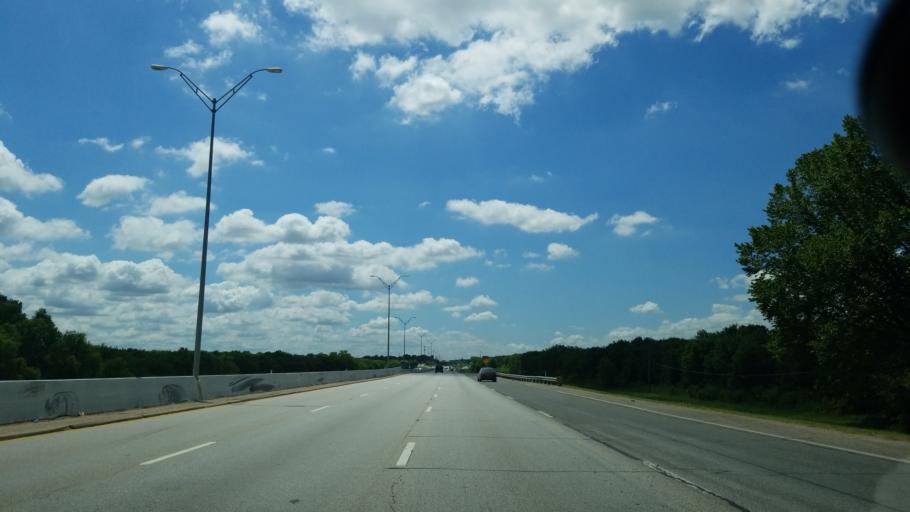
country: US
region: Texas
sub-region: Dallas County
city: Dallas
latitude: 32.7425
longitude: -96.7229
